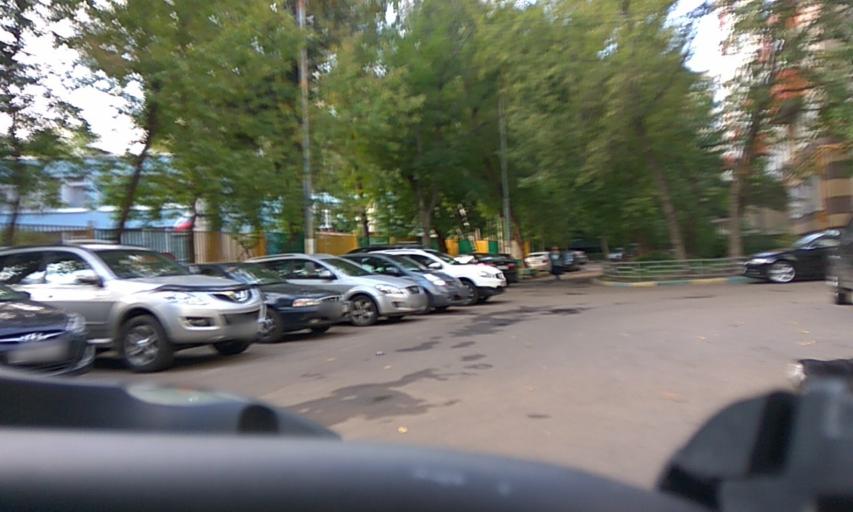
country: RU
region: Moscow
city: Kolomenskoye
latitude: 55.6778
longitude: 37.6846
